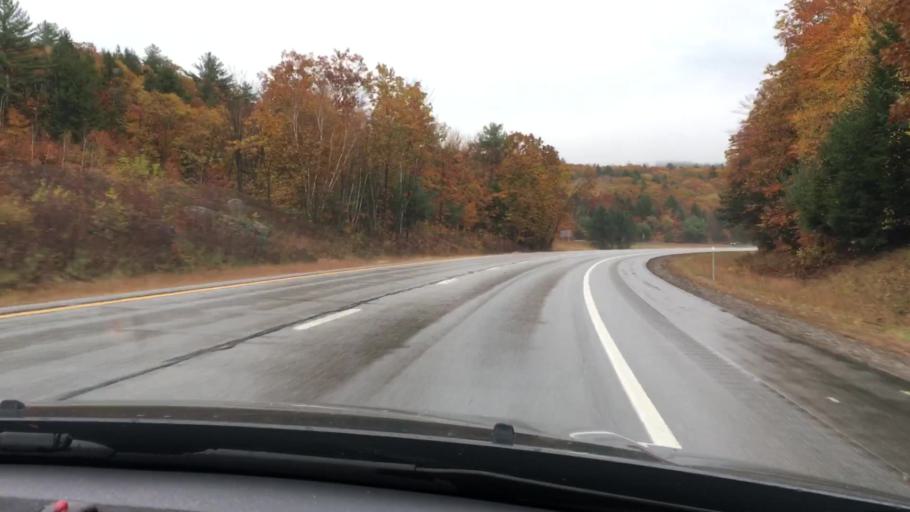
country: US
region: New Hampshire
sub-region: Grafton County
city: Ashland
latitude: 43.5924
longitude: -71.6219
